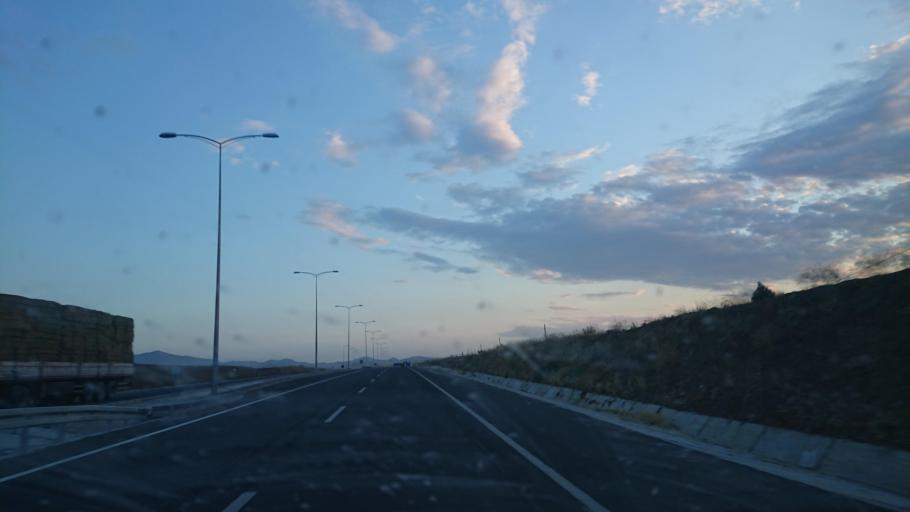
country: TR
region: Aksaray
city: Balci
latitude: 38.7792
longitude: 34.1141
